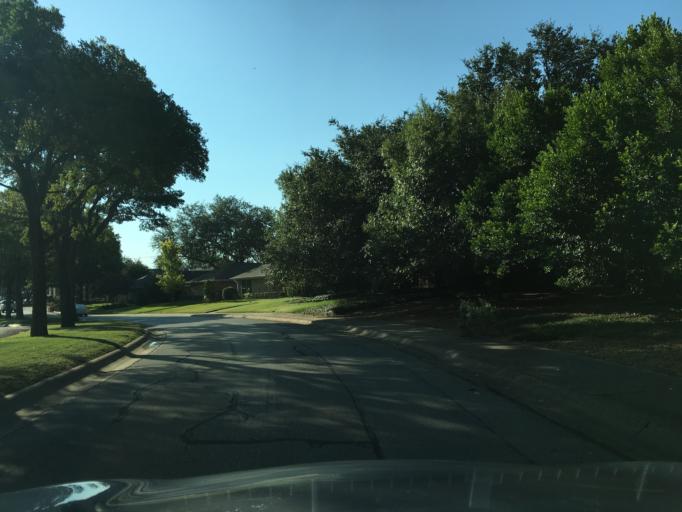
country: US
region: Texas
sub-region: Dallas County
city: Addison
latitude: 32.9605
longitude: -96.8552
